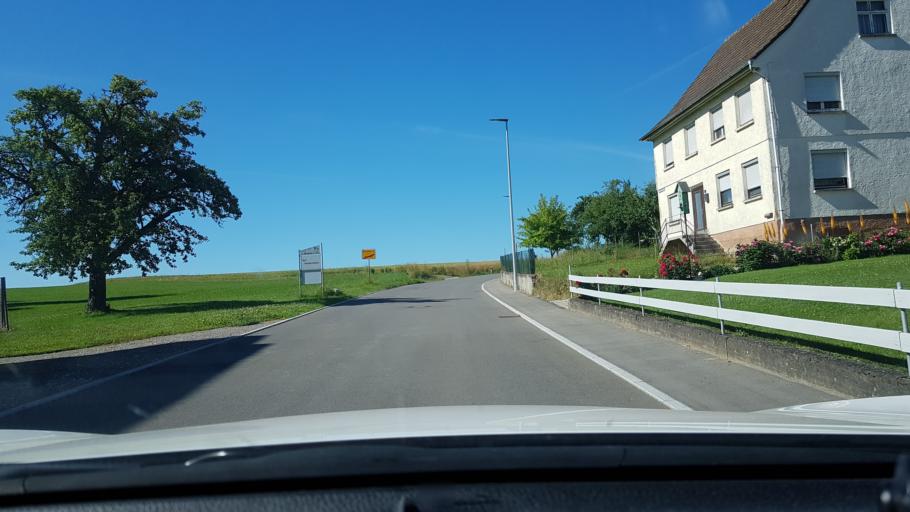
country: DE
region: Baden-Wuerttemberg
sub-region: Tuebingen Region
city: Gutenzell-Hurbel
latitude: 48.1205
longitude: 9.9597
